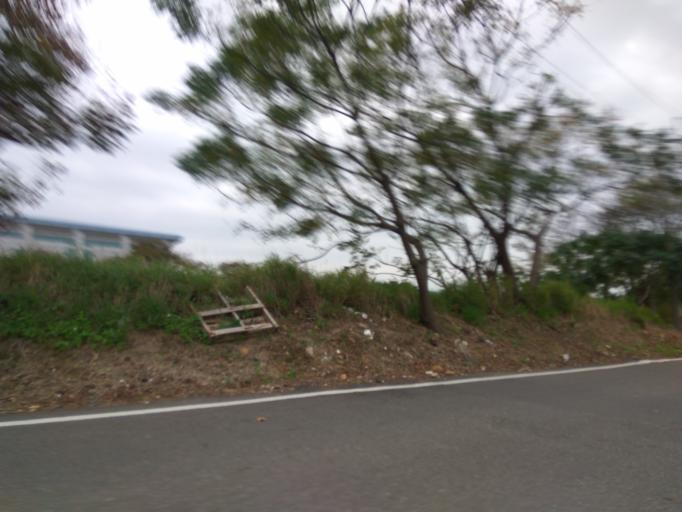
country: TW
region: Taiwan
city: Taoyuan City
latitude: 25.0245
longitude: 121.2241
